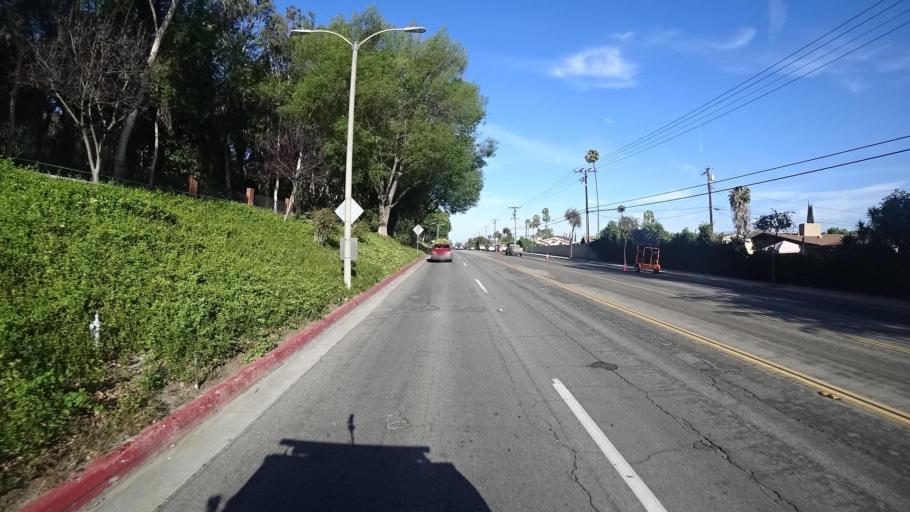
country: US
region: California
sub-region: Los Angeles County
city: South San Jose Hills
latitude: 34.0255
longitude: -117.9242
